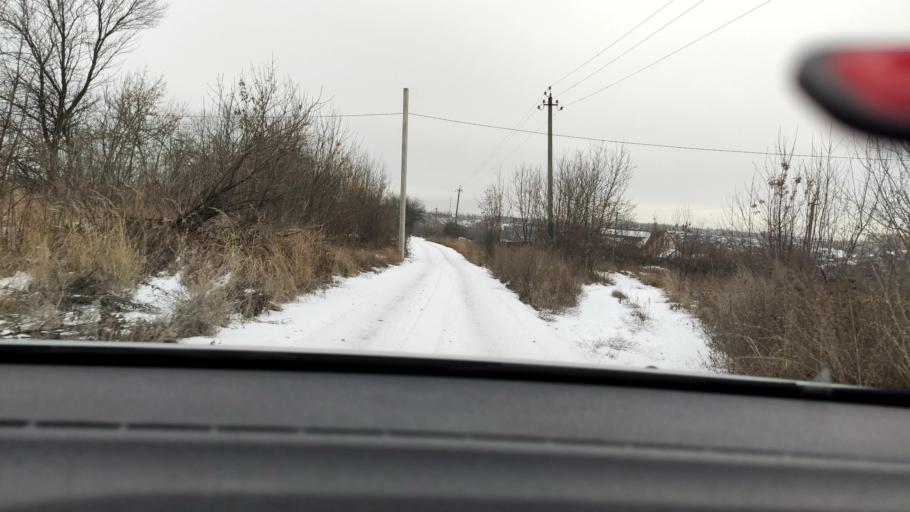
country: RU
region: Voronezj
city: Semiluki
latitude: 51.7031
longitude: 38.9867
